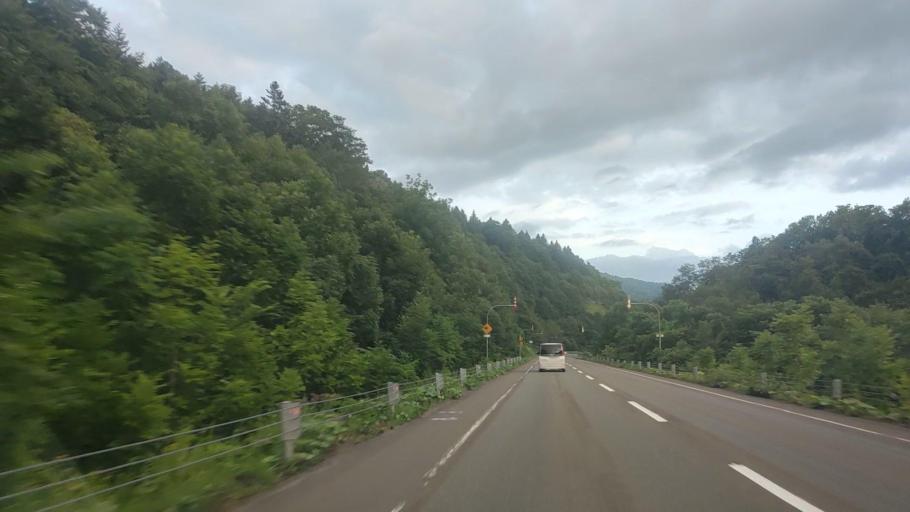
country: JP
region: Hokkaido
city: Shimo-furano
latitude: 43.3583
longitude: 142.2424
